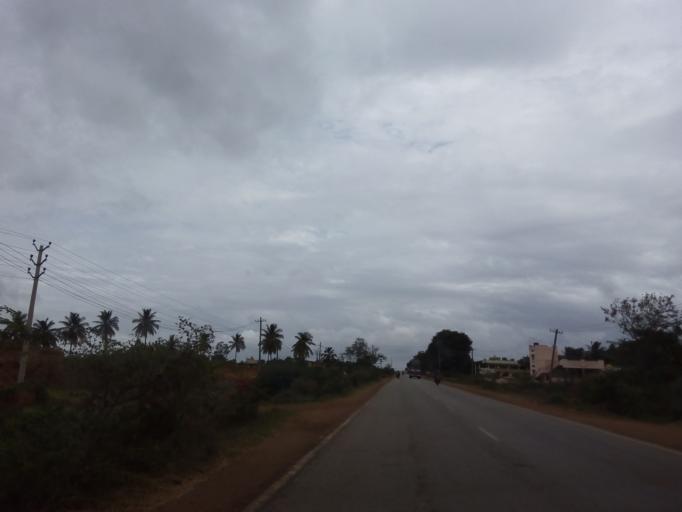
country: IN
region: Karnataka
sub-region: Davanagere
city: Harihar
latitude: 14.5336
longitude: 75.7679
